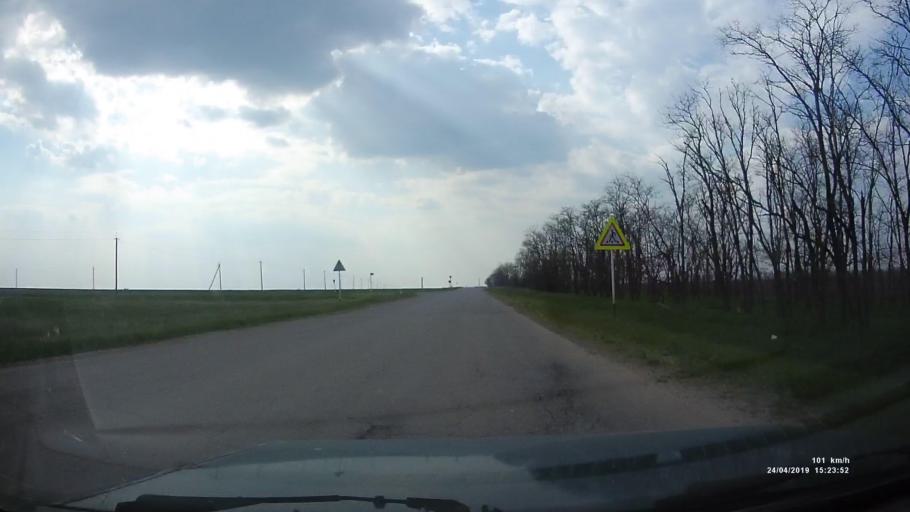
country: RU
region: Rostov
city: Remontnoye
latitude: 46.5453
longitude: 43.0807
